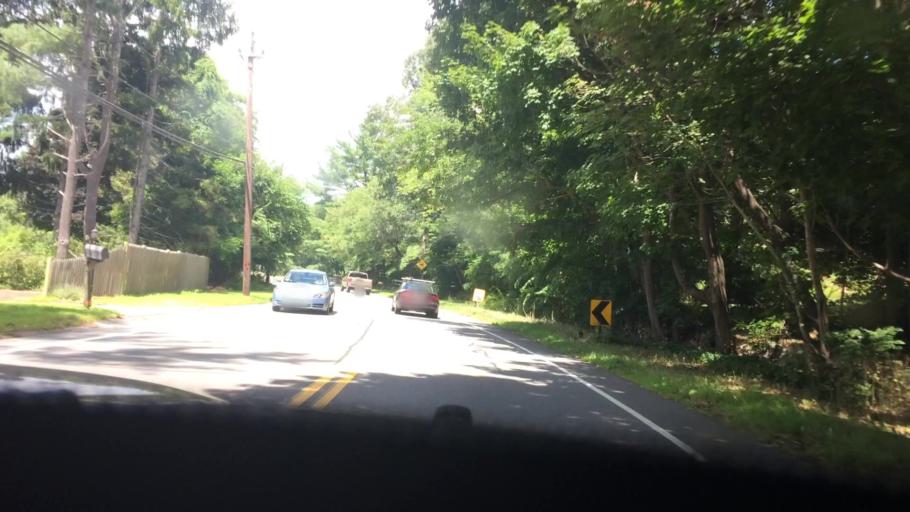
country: US
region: Massachusetts
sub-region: Middlesex County
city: Wayland
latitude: 42.3738
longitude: -71.3733
